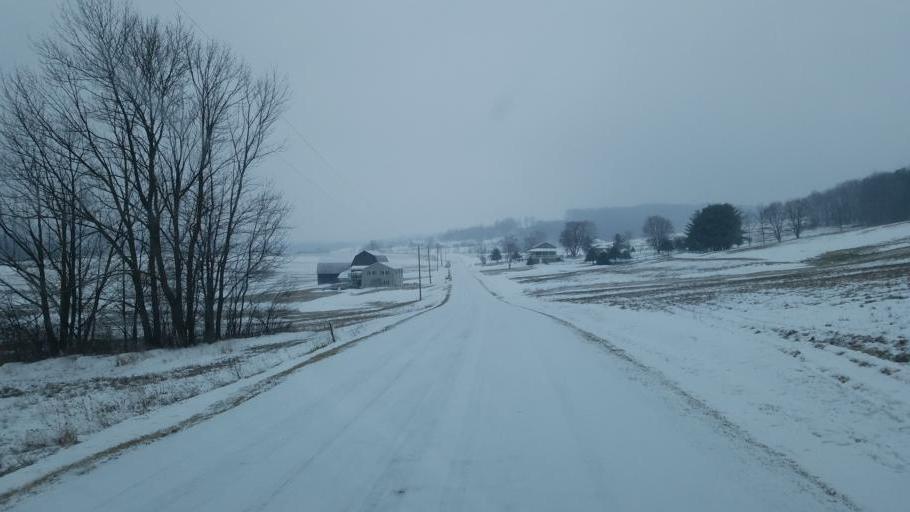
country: US
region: New York
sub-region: Steuben County
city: Canisteo
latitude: 42.1118
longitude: -77.5023
